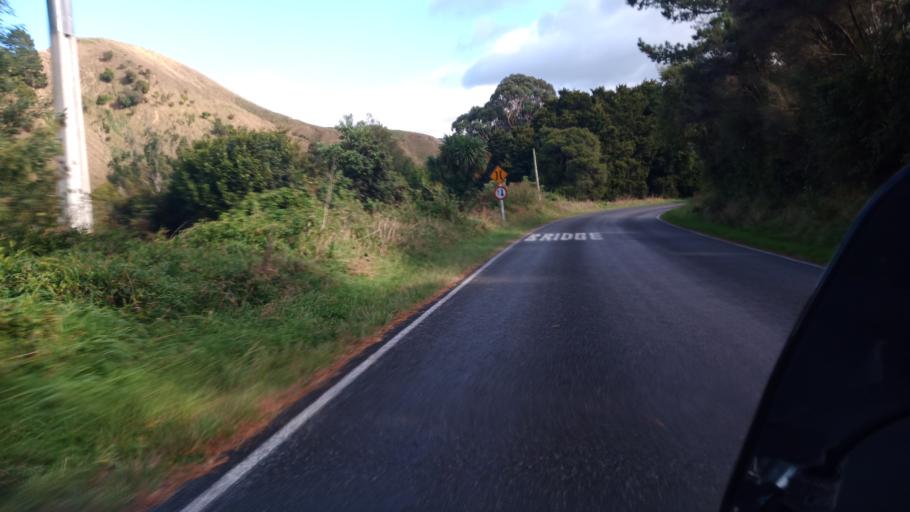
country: NZ
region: Gisborne
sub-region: Gisborne District
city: Gisborne
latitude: -38.5390
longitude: 177.5612
